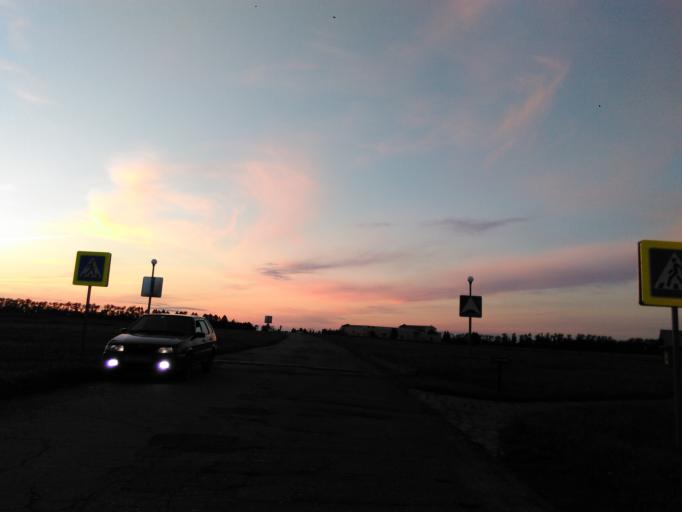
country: RU
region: Penza
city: Lermontovo
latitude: 52.9963
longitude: 43.6730
